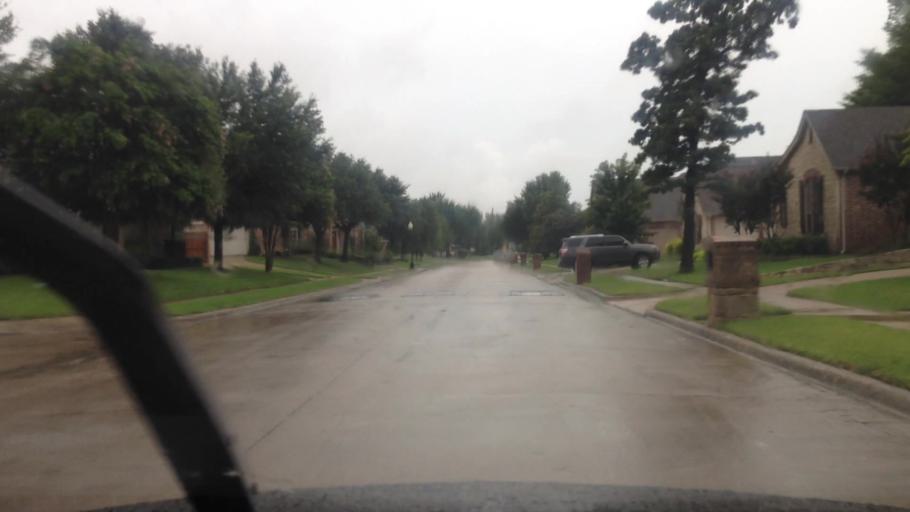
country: US
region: Texas
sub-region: Tarrant County
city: Keller
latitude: 32.9064
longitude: -97.2114
